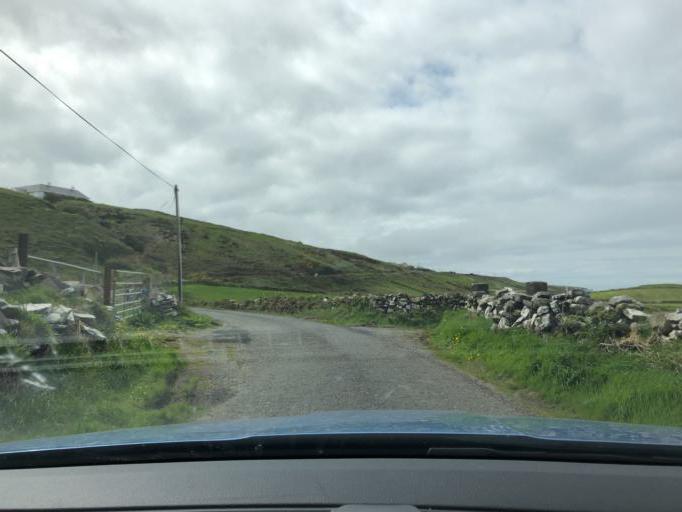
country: IE
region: Connaught
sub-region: County Galway
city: Bearna
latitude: 53.0033
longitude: -9.3909
